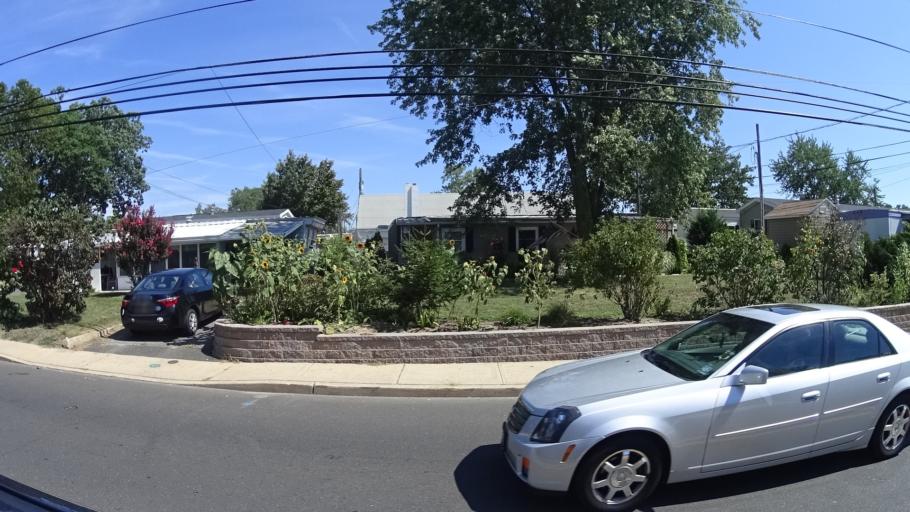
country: US
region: New Jersey
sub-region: Monmouth County
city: Shark River Hills
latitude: 40.2037
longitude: -74.0407
